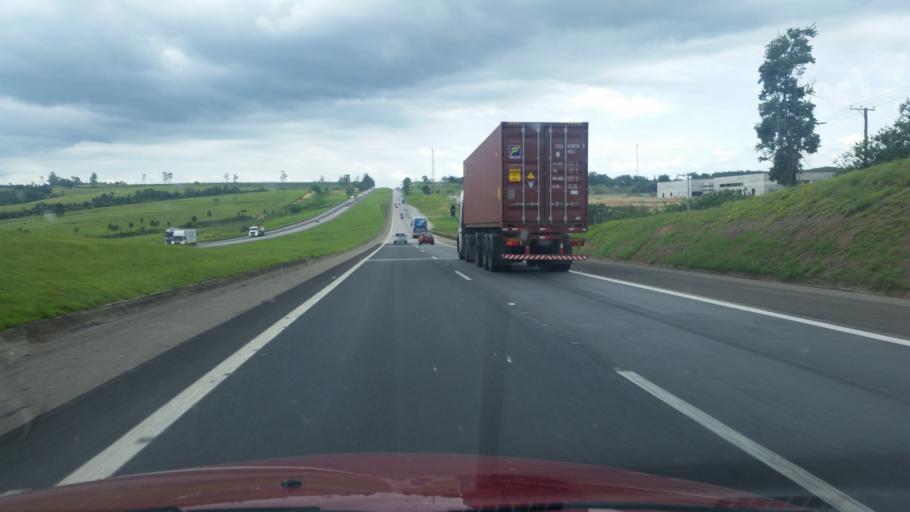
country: BR
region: Sao Paulo
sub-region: Sorocaba
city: Sorocaba
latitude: -23.3730
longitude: -47.4413
